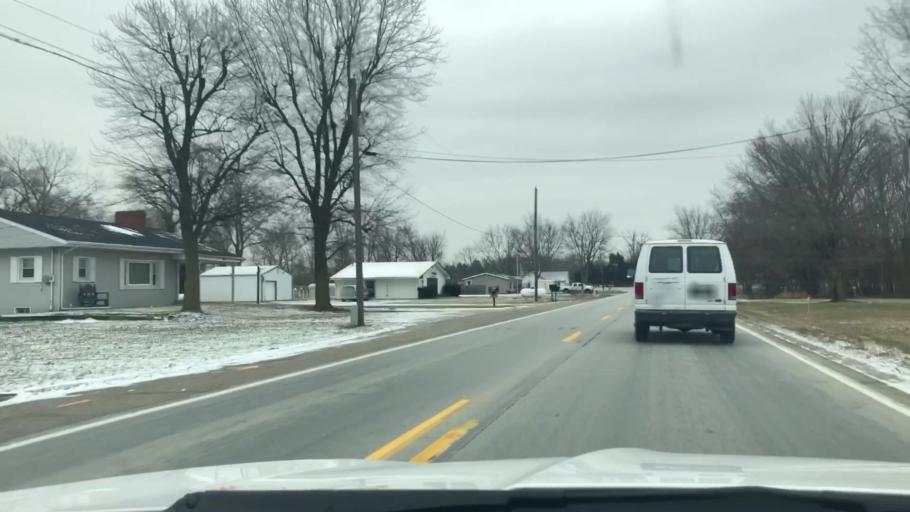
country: US
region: Indiana
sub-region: Fulton County
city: Rochester
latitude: 41.0597
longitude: -86.1709
